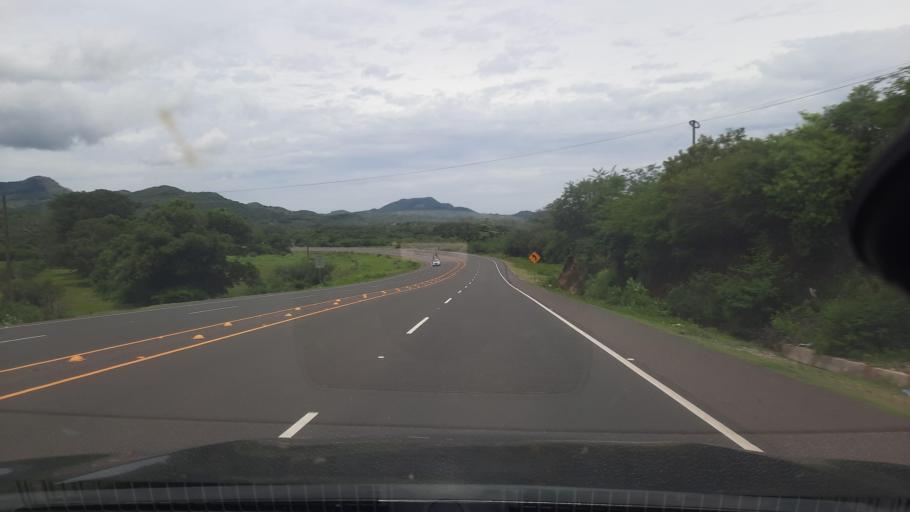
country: HN
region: Valle
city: Aramecina
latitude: 13.7213
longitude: -87.7104
